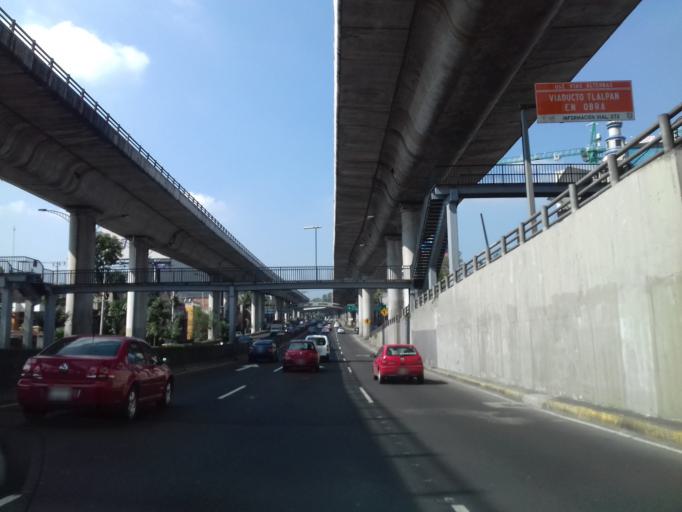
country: MX
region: Mexico City
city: Magdalena Contreras
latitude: 19.3379
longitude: -99.2048
